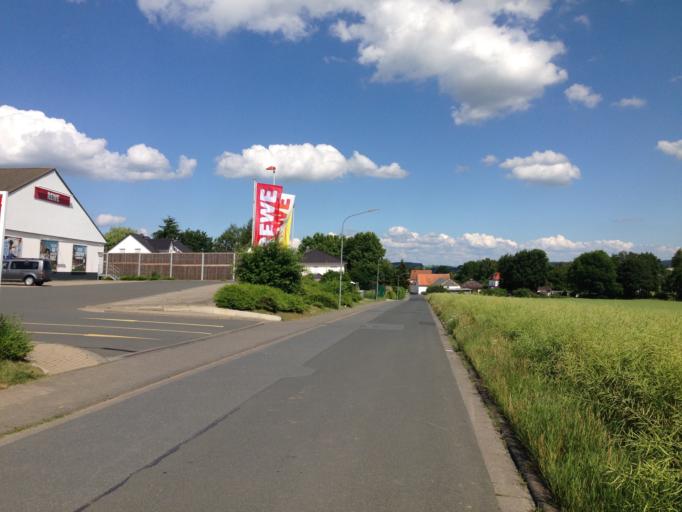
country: DE
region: Hesse
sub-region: Regierungsbezirk Giessen
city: Hoernsheim
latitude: 50.5174
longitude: 8.6192
